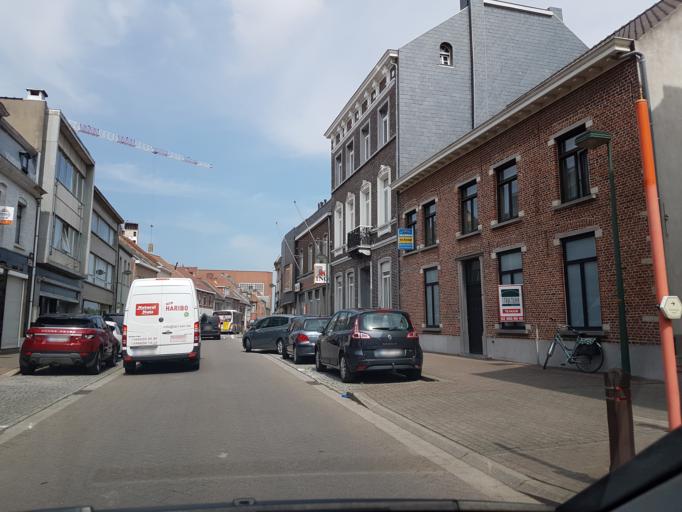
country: BE
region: Flanders
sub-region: Provincie Vlaams-Brabant
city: Merchtem
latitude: 50.9597
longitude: 4.2324
